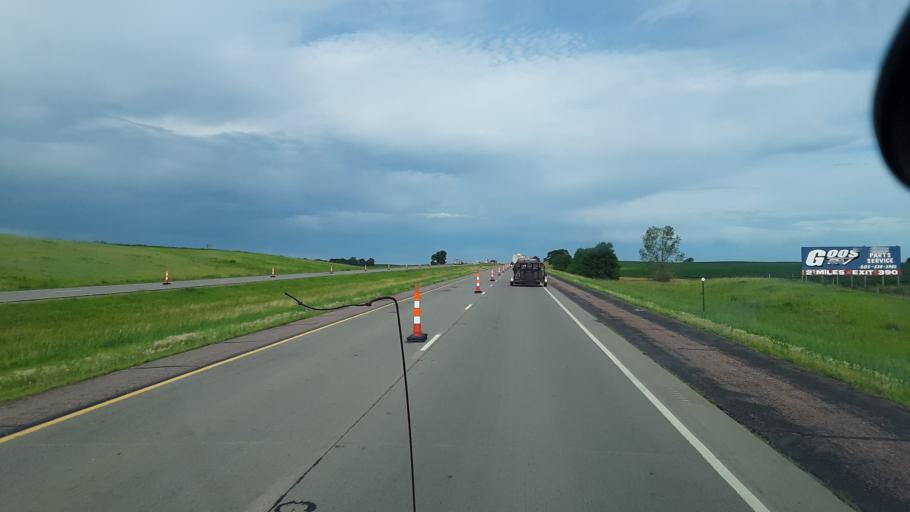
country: US
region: South Dakota
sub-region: Minnehaha County
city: Crooks
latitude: 43.6087
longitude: -96.8455
